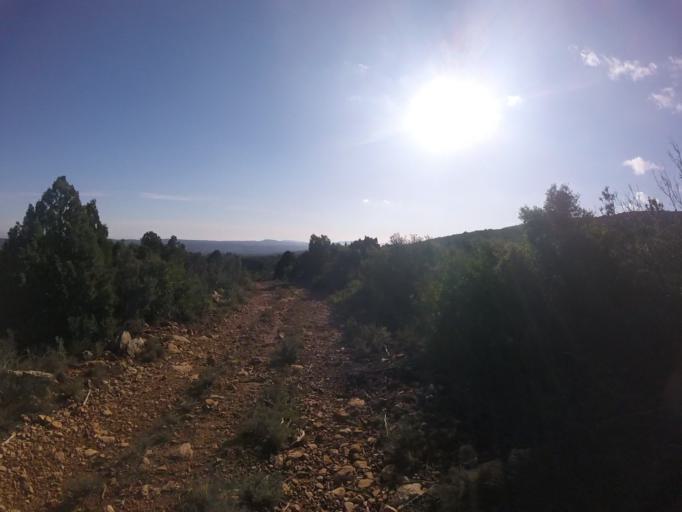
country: ES
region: Valencia
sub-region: Provincia de Castello
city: Sarratella
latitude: 40.2962
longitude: 0.0475
